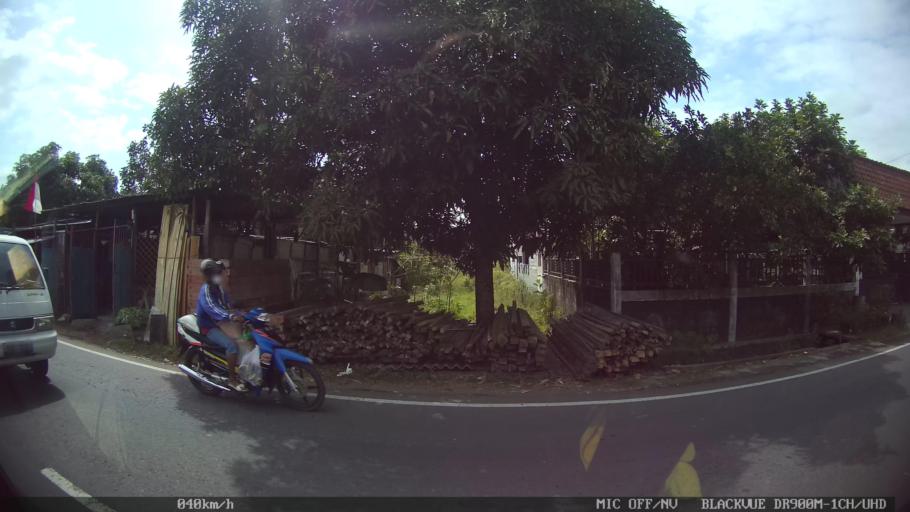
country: ID
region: Central Java
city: Candi Prambanan
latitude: -7.8267
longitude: 110.4789
